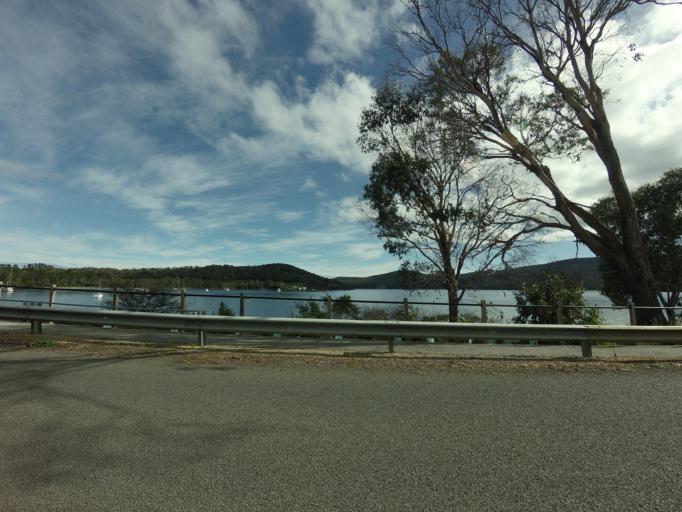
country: AU
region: Tasmania
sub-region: Clarence
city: Sandford
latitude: -43.1020
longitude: 147.7421
